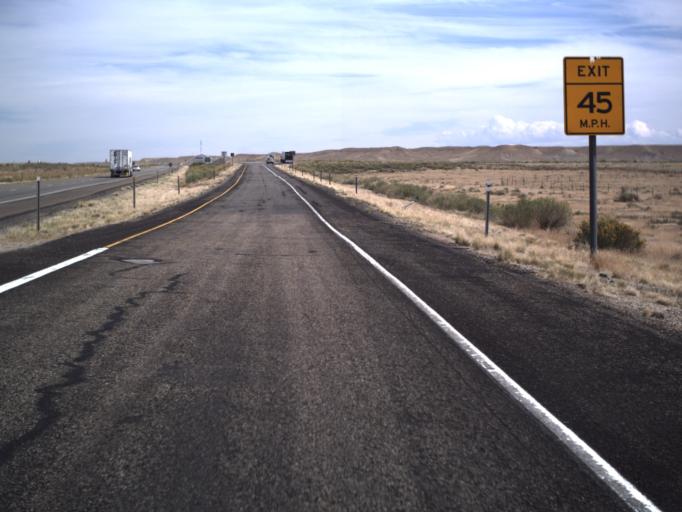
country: US
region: Utah
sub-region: Grand County
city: Moab
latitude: 38.9535
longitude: -109.7590
